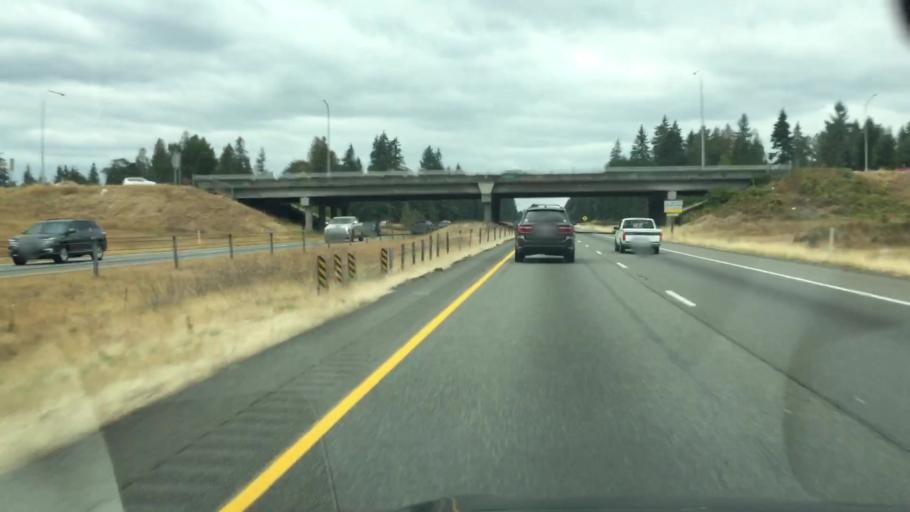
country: US
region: Washington
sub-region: Pierce County
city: Summit
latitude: 47.1581
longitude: -122.3557
